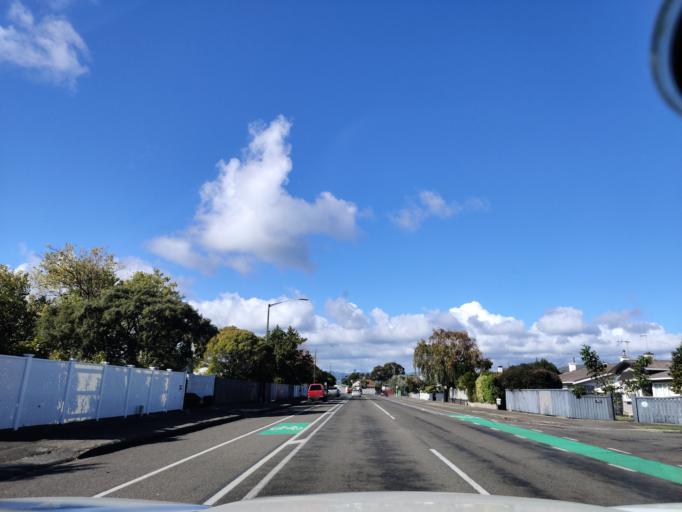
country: NZ
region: Manawatu-Wanganui
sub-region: Palmerston North City
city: Palmerston North
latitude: -40.3514
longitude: 175.5985
